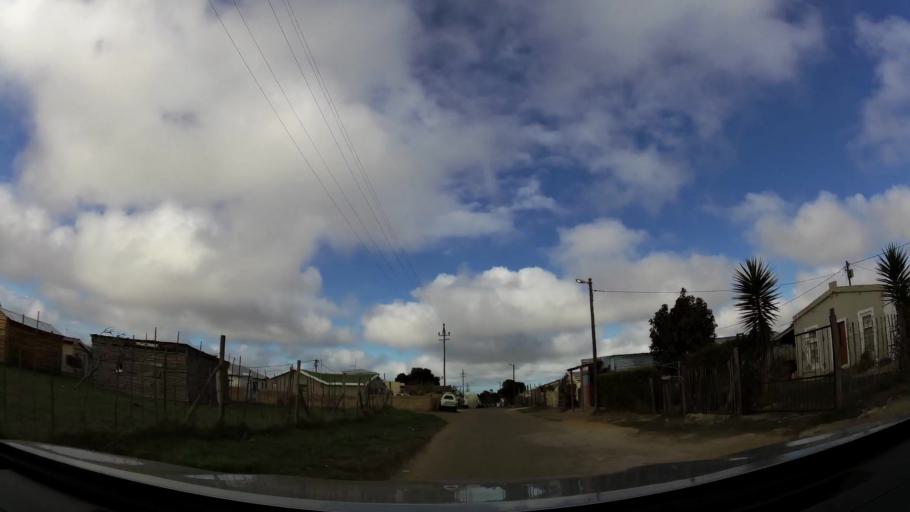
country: ZA
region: Western Cape
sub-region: Eden District Municipality
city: Plettenberg Bay
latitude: -34.0474
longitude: 23.3263
